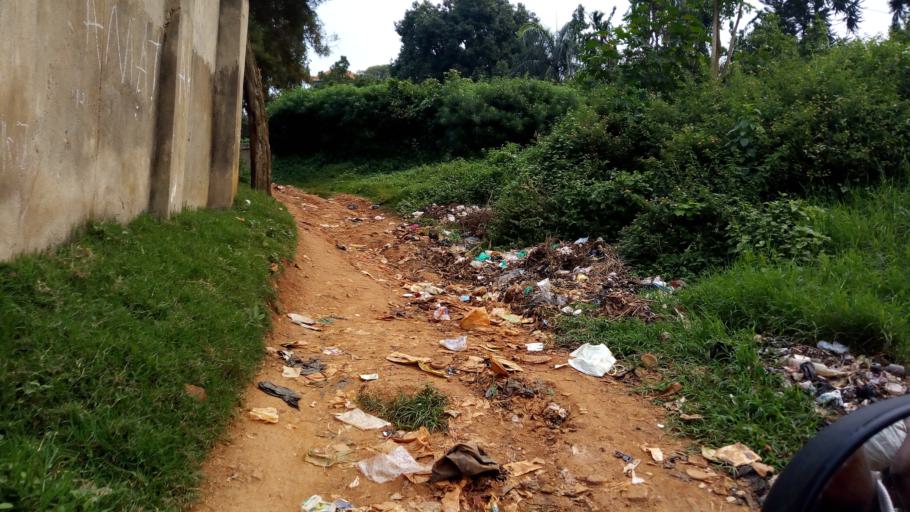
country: UG
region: Central Region
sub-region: Wakiso District
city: Kireka
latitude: 0.3286
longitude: 32.6347
